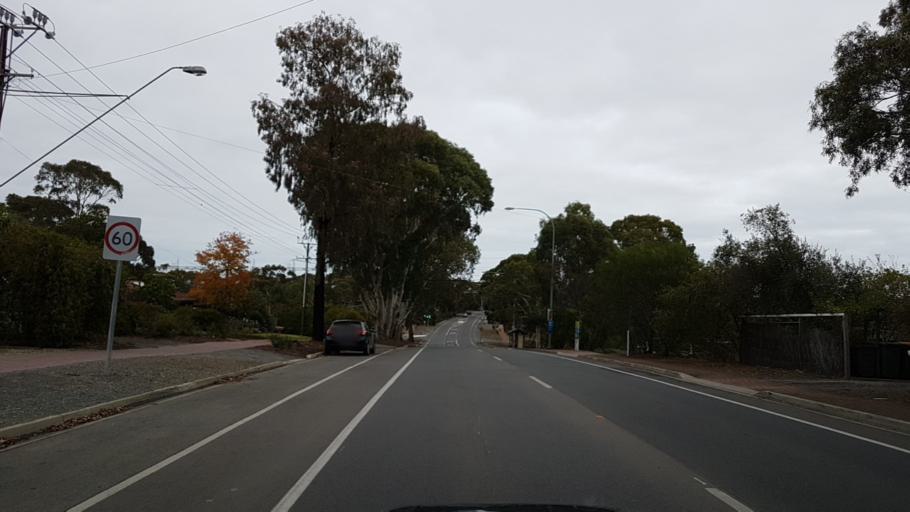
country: AU
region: South Australia
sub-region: Onkaparinga
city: Bedford Park
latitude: -35.0496
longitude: 138.5810
